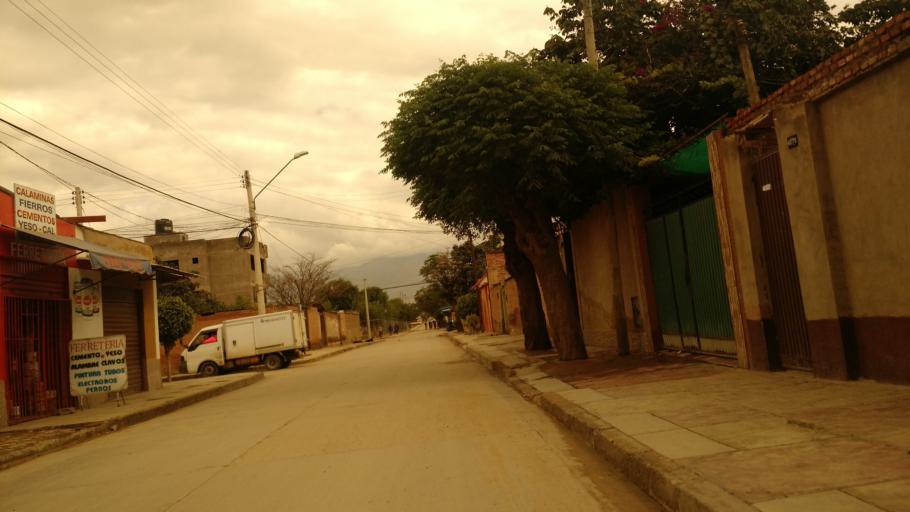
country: BO
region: Cochabamba
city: Cochabamba
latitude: -17.4409
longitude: -66.1556
